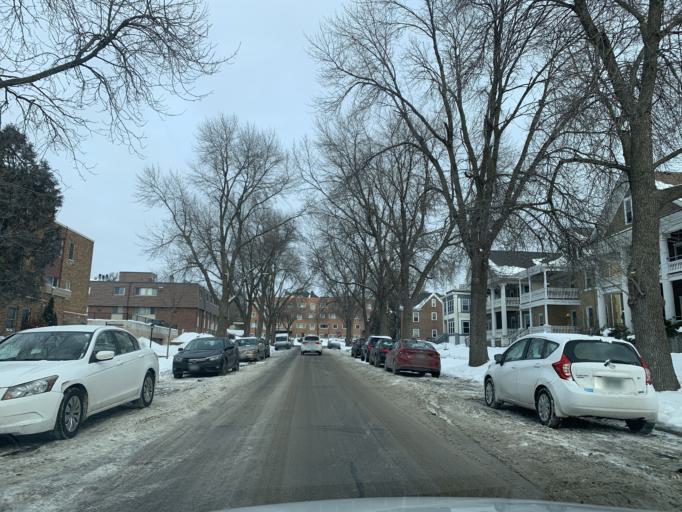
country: US
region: Minnesota
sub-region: Hennepin County
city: Minneapolis
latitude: 44.9616
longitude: -93.2829
